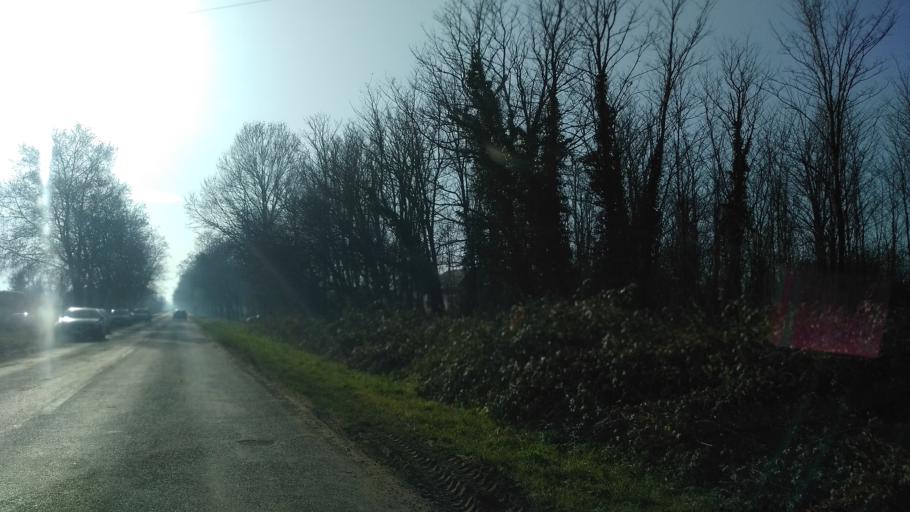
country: HU
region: Somogy
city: Barcs
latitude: 45.9732
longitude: 17.4586
